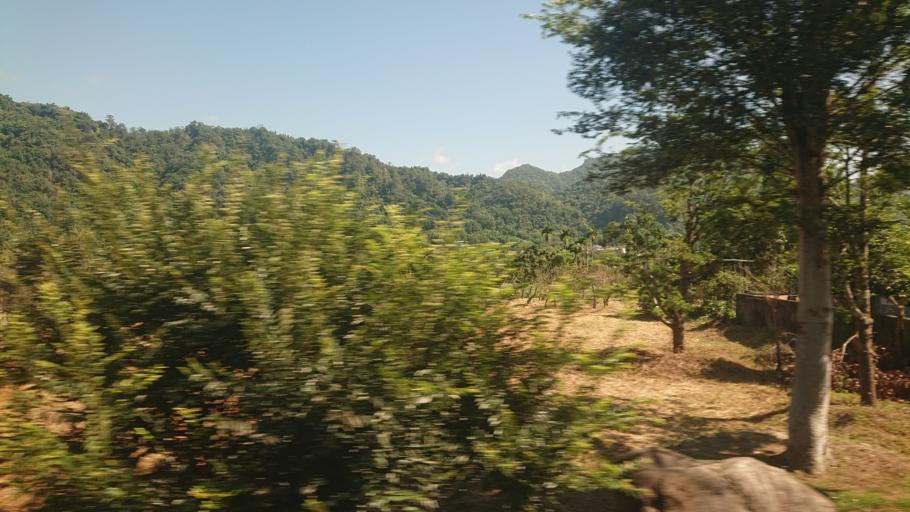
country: TW
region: Taiwan
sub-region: Nantou
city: Puli
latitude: 24.0591
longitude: 120.9370
